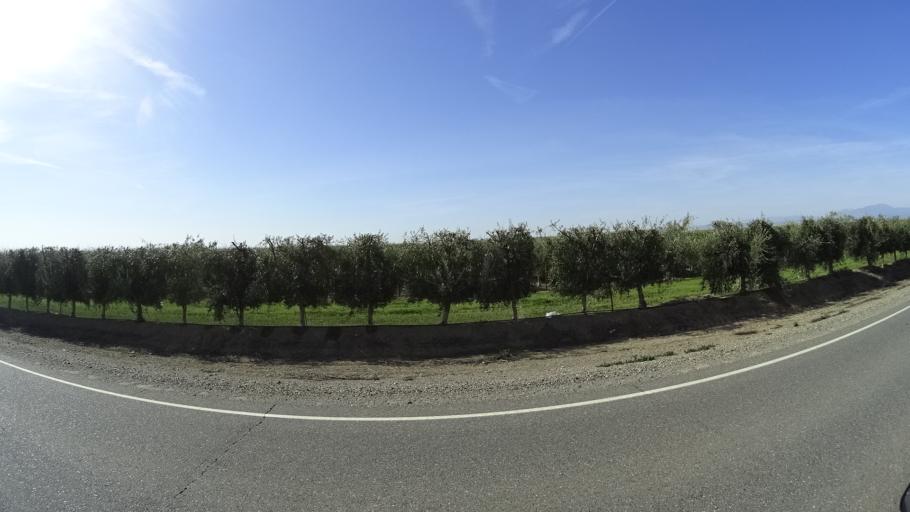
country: US
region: California
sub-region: Glenn County
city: Willows
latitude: 39.6245
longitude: -122.2248
